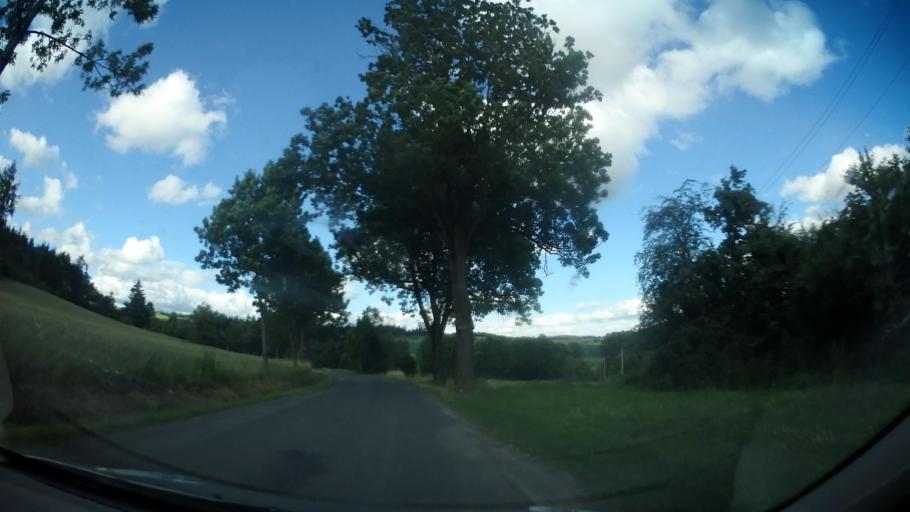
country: CZ
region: Vysocina
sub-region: Okres Zd'ar nad Sazavou
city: Jimramov
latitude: 49.5658
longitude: 16.1795
